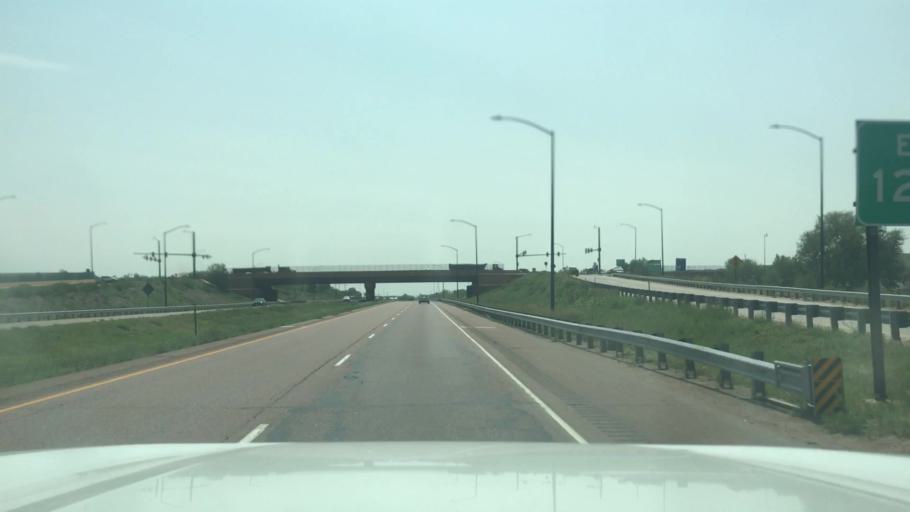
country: US
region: Colorado
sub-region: El Paso County
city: Fountain
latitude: 38.6747
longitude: -104.7106
